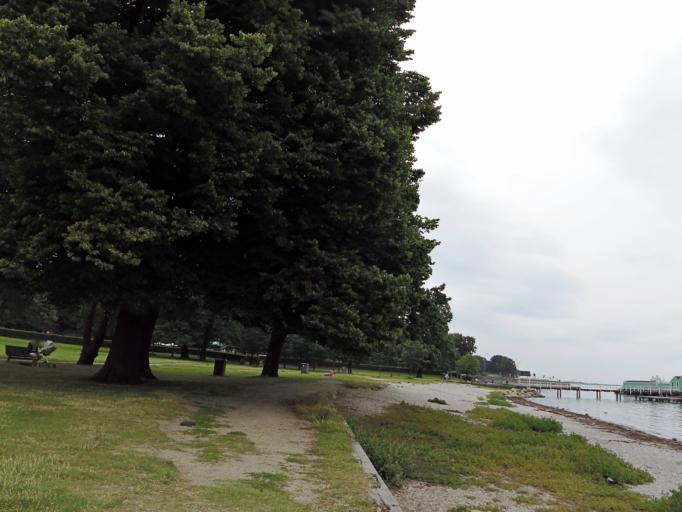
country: DK
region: Capital Region
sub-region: Gentofte Kommune
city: Charlottenlund
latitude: 55.7485
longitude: 12.5897
